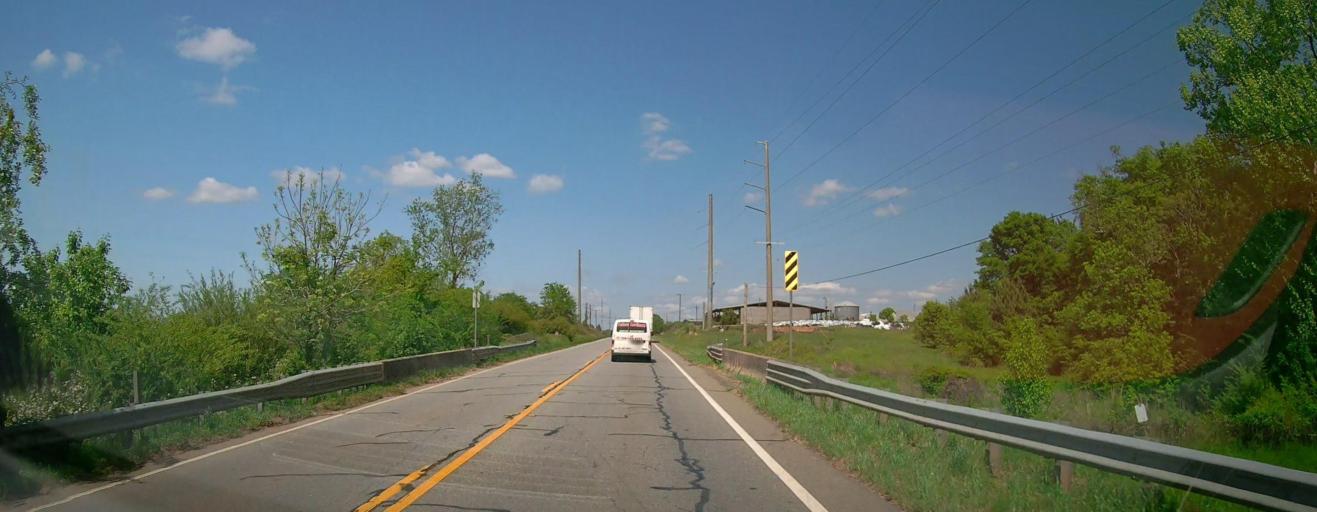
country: US
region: Georgia
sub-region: Putnam County
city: Eatonton
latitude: 33.3445
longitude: -83.3603
